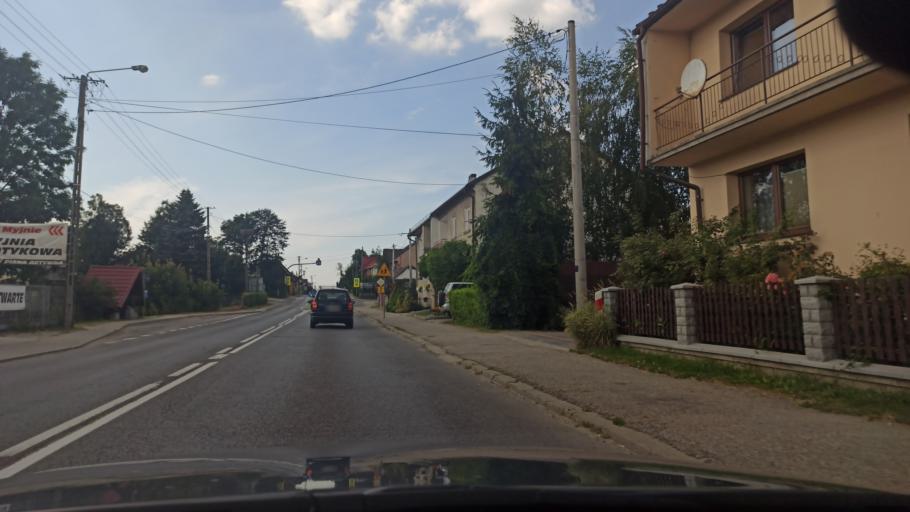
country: PL
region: Lesser Poland Voivodeship
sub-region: Powiat nowotarski
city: Waksmund
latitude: 49.4805
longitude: 20.0795
